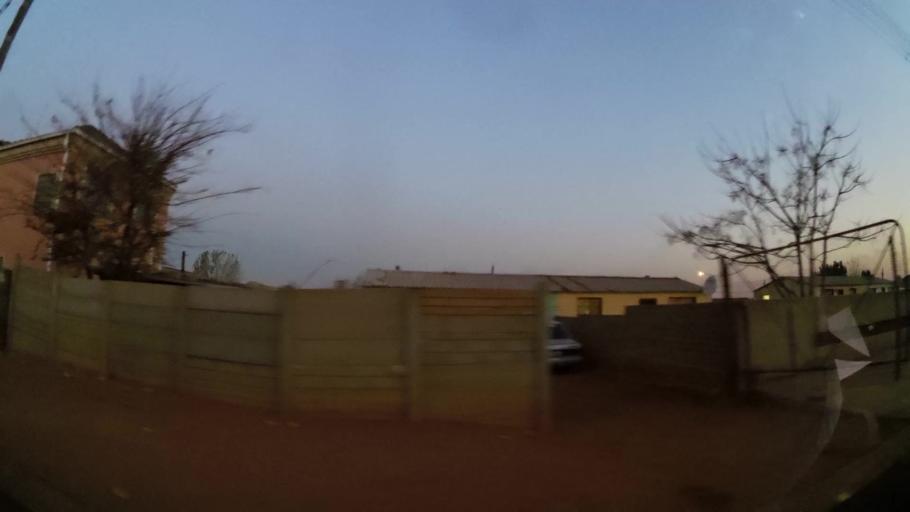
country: ZA
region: Gauteng
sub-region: West Rand District Municipality
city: Randfontein
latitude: -26.2082
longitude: 27.7105
